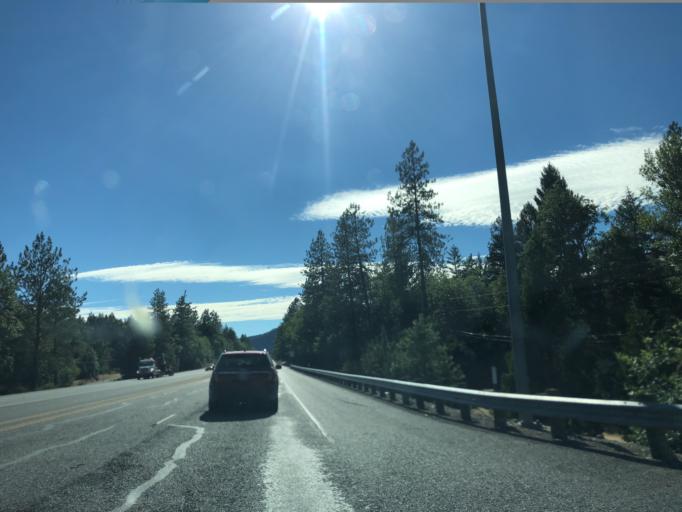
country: US
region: Oregon
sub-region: Josephine County
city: Redwood
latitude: 42.4126
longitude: -123.4124
